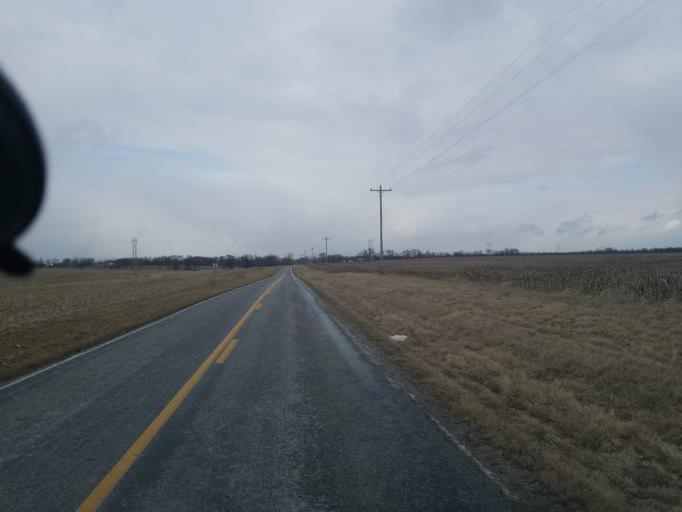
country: US
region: Missouri
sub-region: Boone County
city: Hallsville
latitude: 39.2471
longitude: -92.2927
